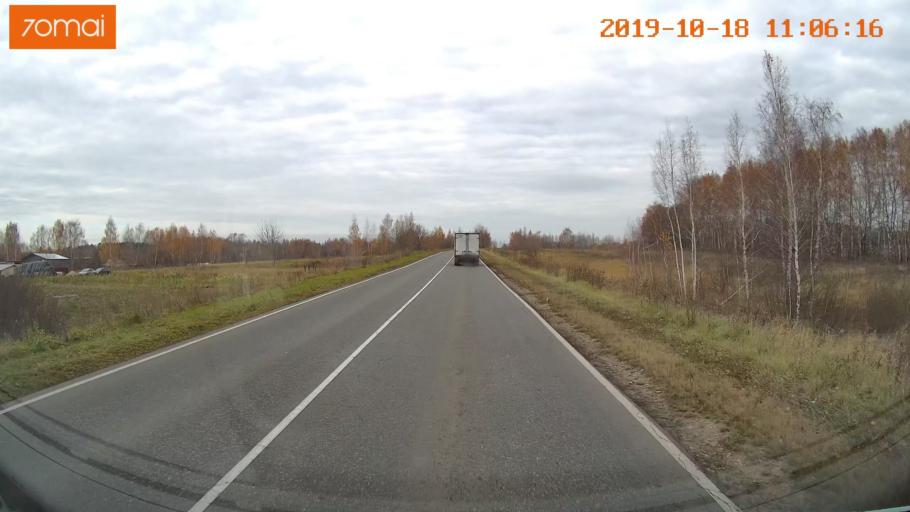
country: RU
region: Tula
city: Kimovsk
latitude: 53.9174
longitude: 38.5397
